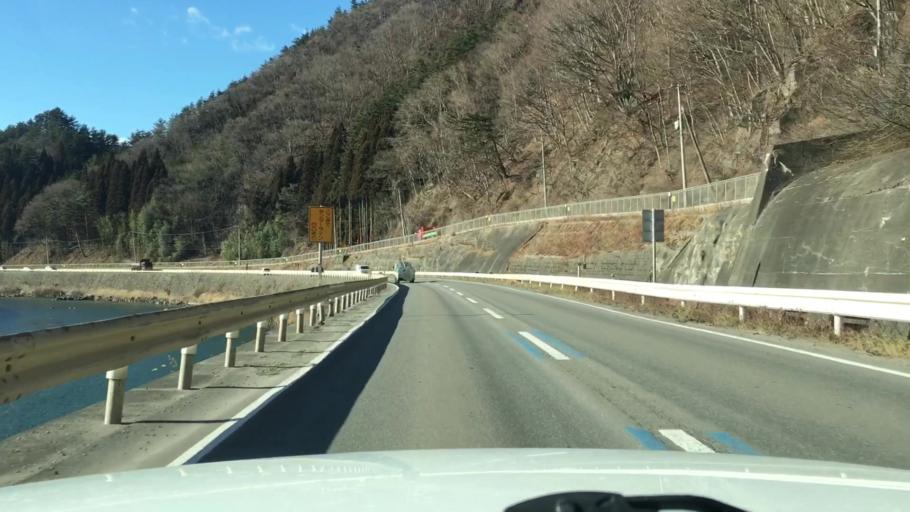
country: JP
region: Iwate
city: Miyako
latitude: 39.6355
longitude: 141.8471
